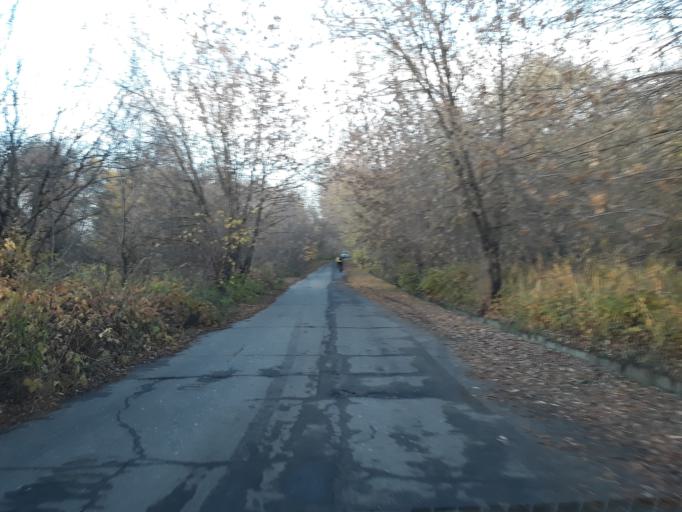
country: RU
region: Nizjnij Novgorod
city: Nizhniy Novgorod
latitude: 56.2801
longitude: 43.9695
